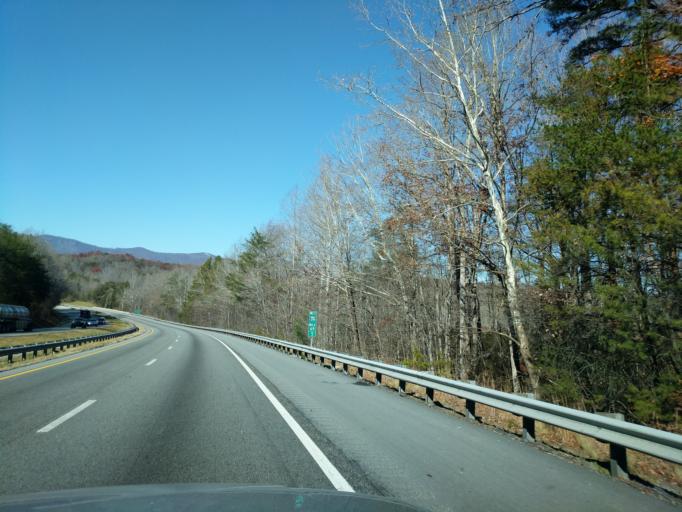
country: US
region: South Carolina
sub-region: Spartanburg County
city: Landrum
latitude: 35.2105
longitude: -82.1823
